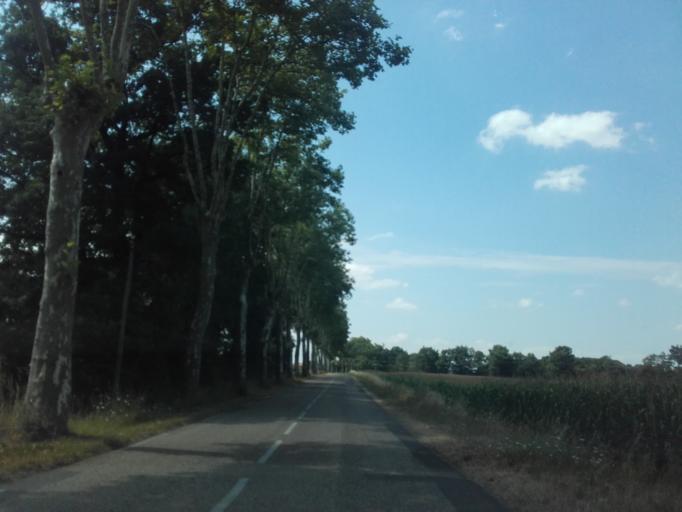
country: FR
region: Rhone-Alpes
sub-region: Departement de l'Ain
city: Chalamont
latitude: 46.0060
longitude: 5.1625
